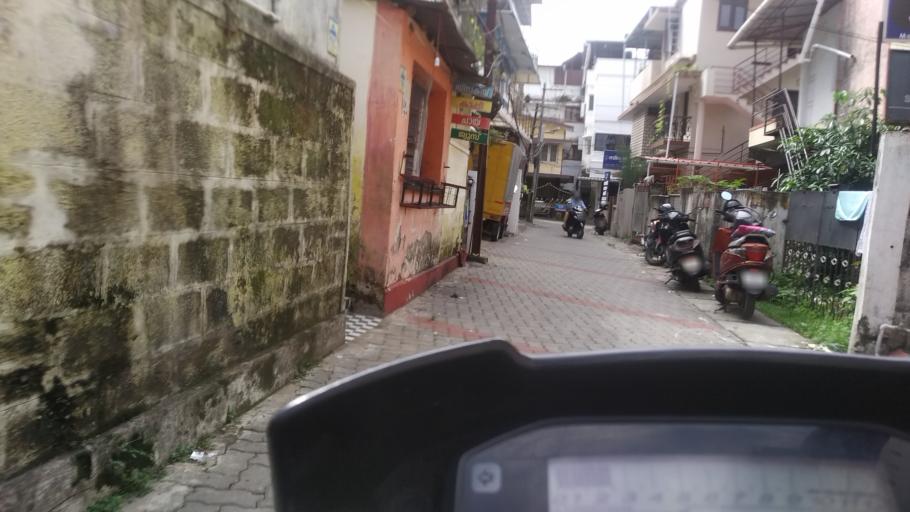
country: IN
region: Kerala
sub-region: Ernakulam
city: Cochin
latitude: 9.9872
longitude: 76.2807
